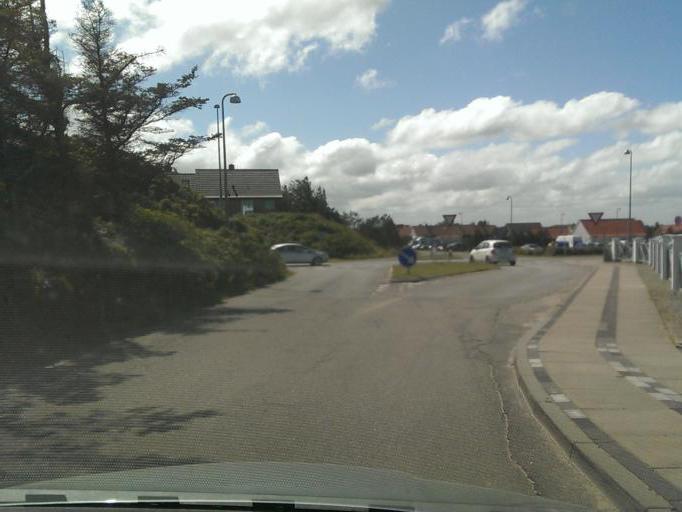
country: DK
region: North Denmark
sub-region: Jammerbugt Kommune
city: Pandrup
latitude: 57.2515
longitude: 9.5911
